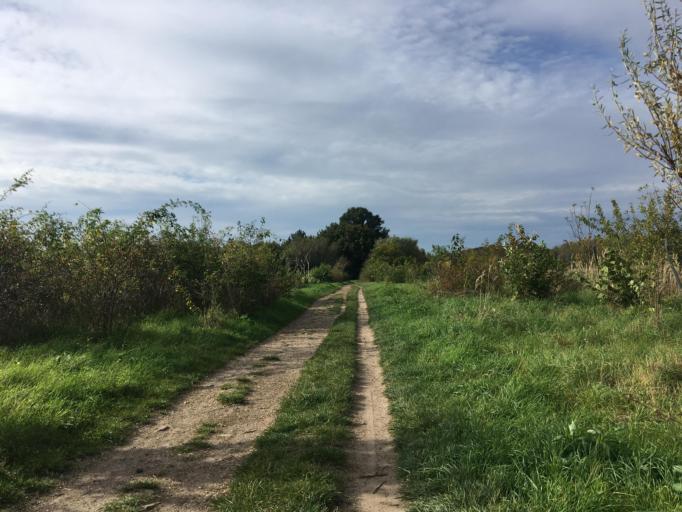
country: DE
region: Berlin
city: Marienfelde
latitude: 52.3932
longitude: 13.3739
